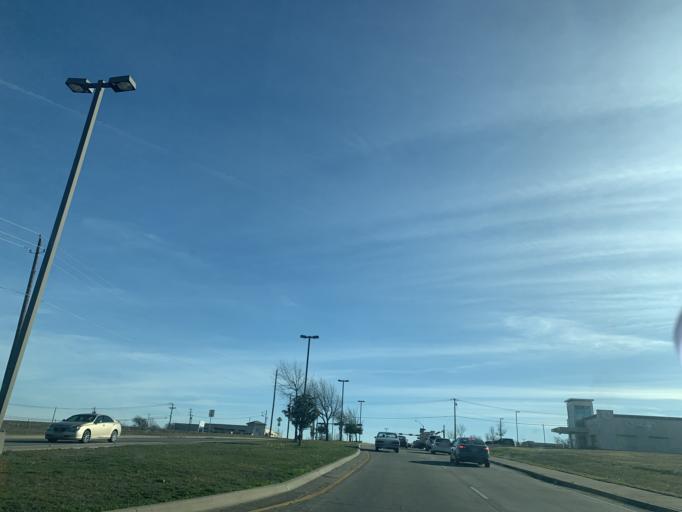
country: US
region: Texas
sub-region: Dallas County
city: Shamrock
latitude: 32.5897
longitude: -96.8761
